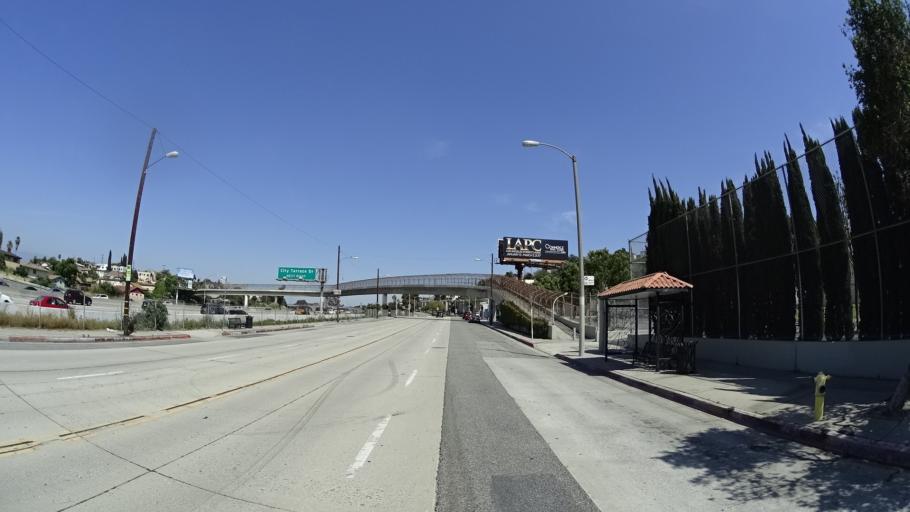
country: US
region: California
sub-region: Los Angeles County
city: Belvedere
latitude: 34.0549
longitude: -118.1890
